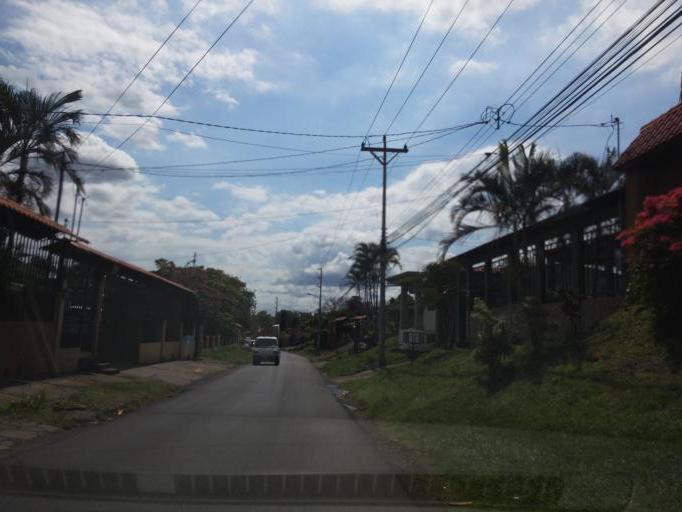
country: CR
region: Alajuela
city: Alajuela
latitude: 10.0190
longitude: -84.1804
